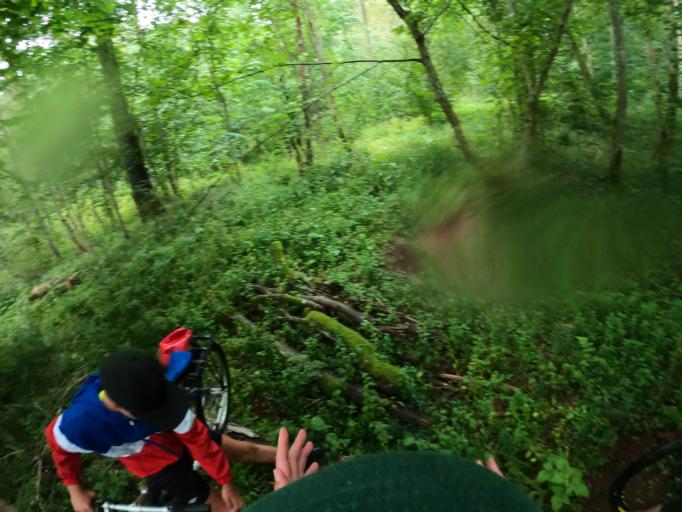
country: LT
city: Raseiniai
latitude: 55.4502
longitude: 23.2005
